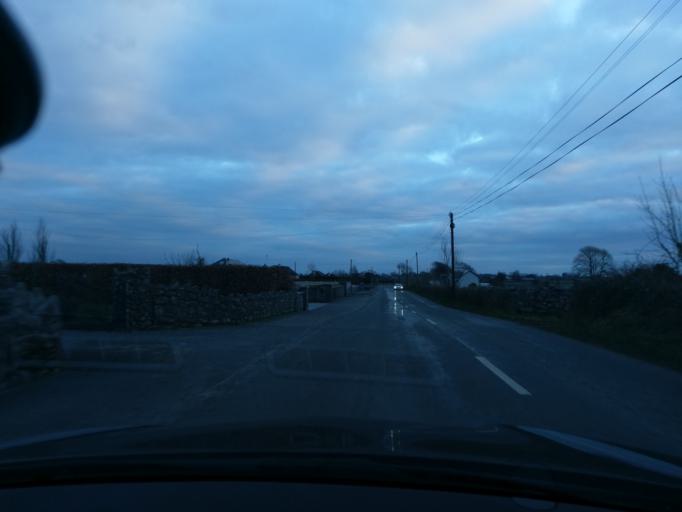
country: IE
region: Connaught
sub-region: County Galway
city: Athenry
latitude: 53.3280
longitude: -8.7661
